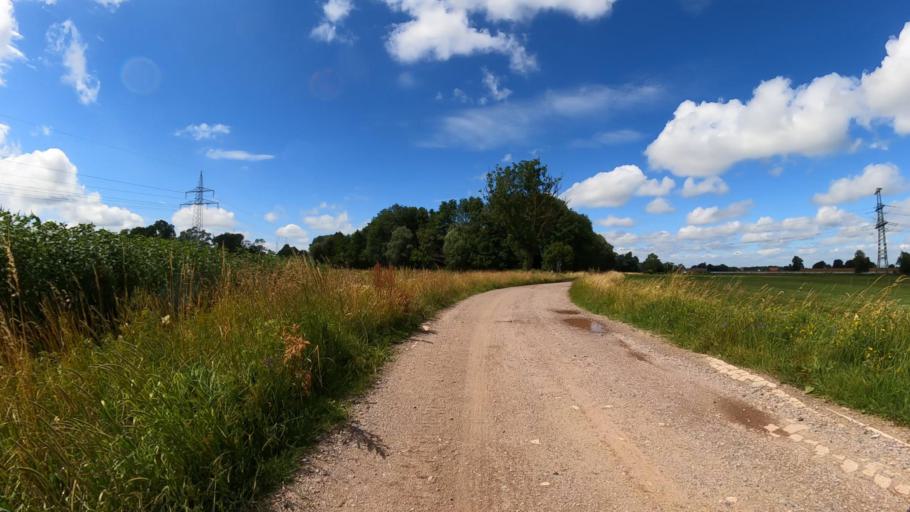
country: DE
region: Lower Saxony
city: Neu Wulmstorf
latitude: 53.4826
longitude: 9.7552
